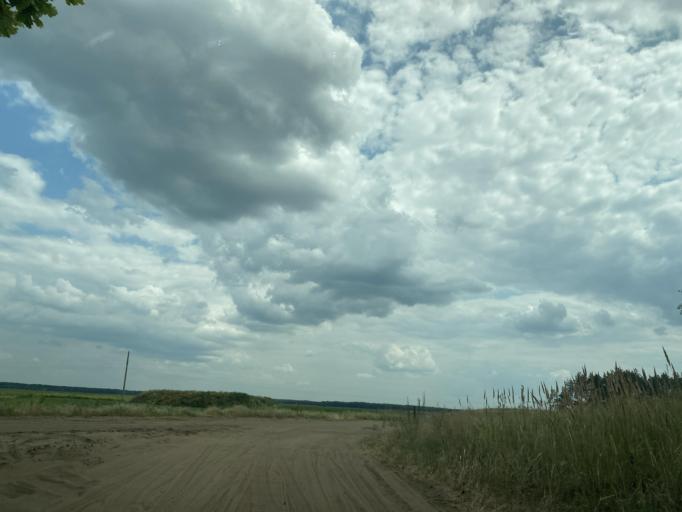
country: BY
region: Brest
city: Ivanava
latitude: 52.3656
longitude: 25.6363
